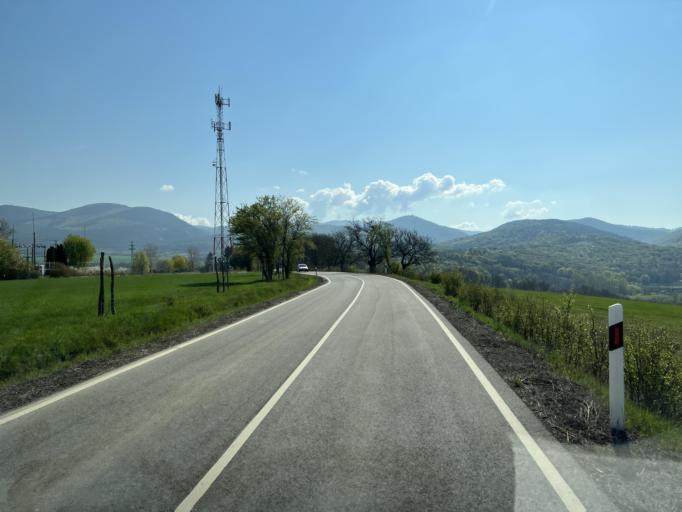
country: HU
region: Pest
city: Szob
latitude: 47.9368
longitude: 18.8111
